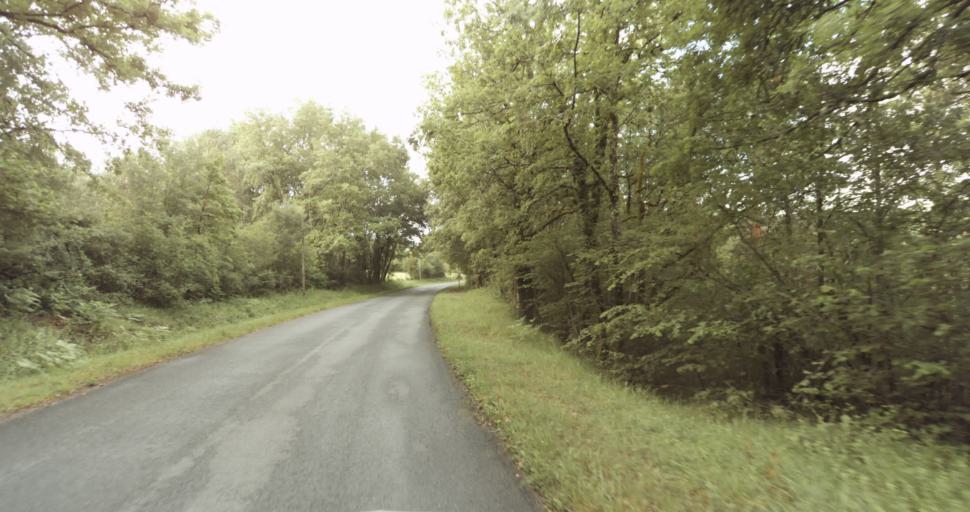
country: FR
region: Aquitaine
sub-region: Departement de la Dordogne
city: Lalinde
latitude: 44.9134
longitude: 0.7940
